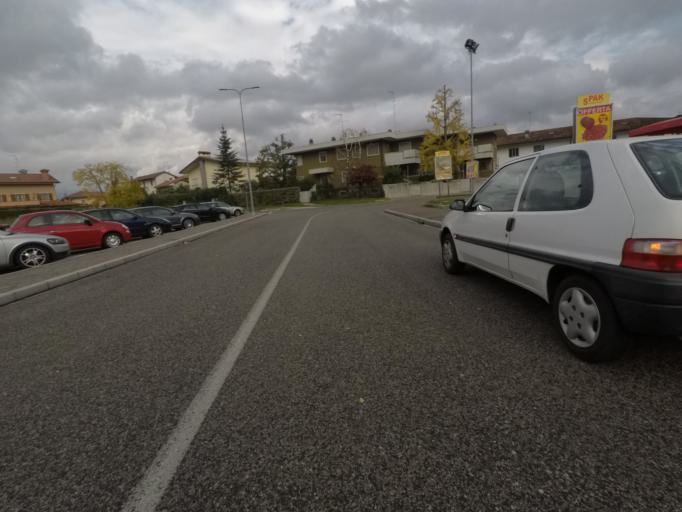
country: IT
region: Friuli Venezia Giulia
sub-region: Provincia di Udine
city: Colugna
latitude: 46.0724
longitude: 13.2169
